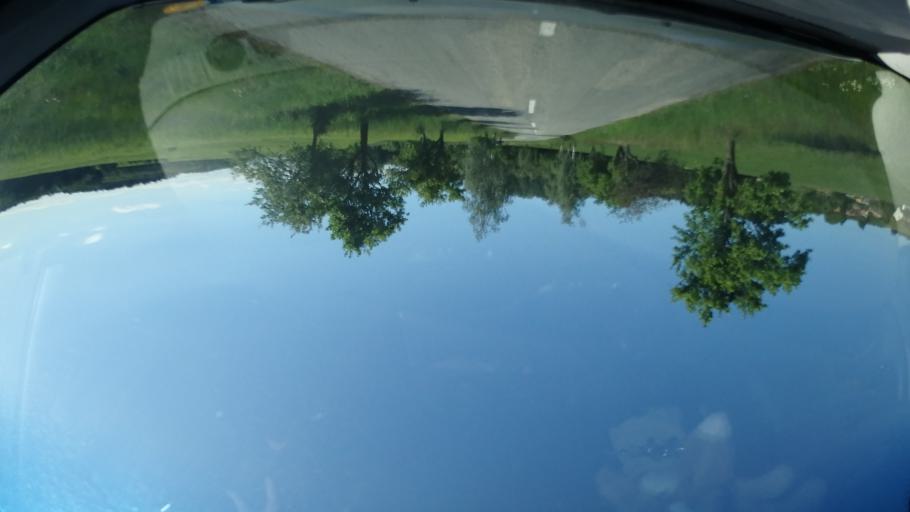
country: CZ
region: South Moravian
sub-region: Okres Blansko
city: Letovice
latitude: 49.5955
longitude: 16.5971
